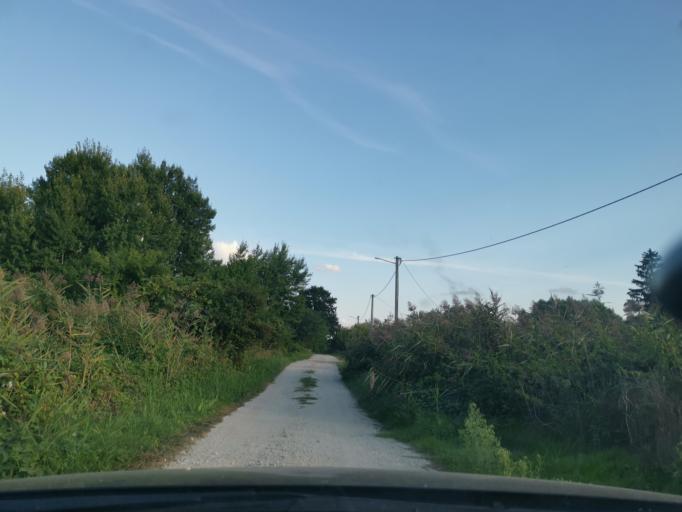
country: SK
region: Trnavsky
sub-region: Okres Senica
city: Senica
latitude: 48.6560
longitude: 17.2603
